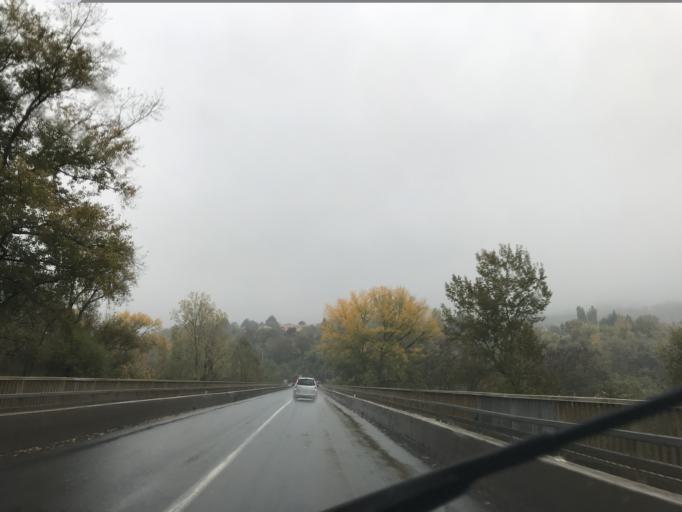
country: FR
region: Auvergne
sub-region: Departement du Puy-de-Dome
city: Dallet
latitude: 45.7746
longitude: 3.2372
